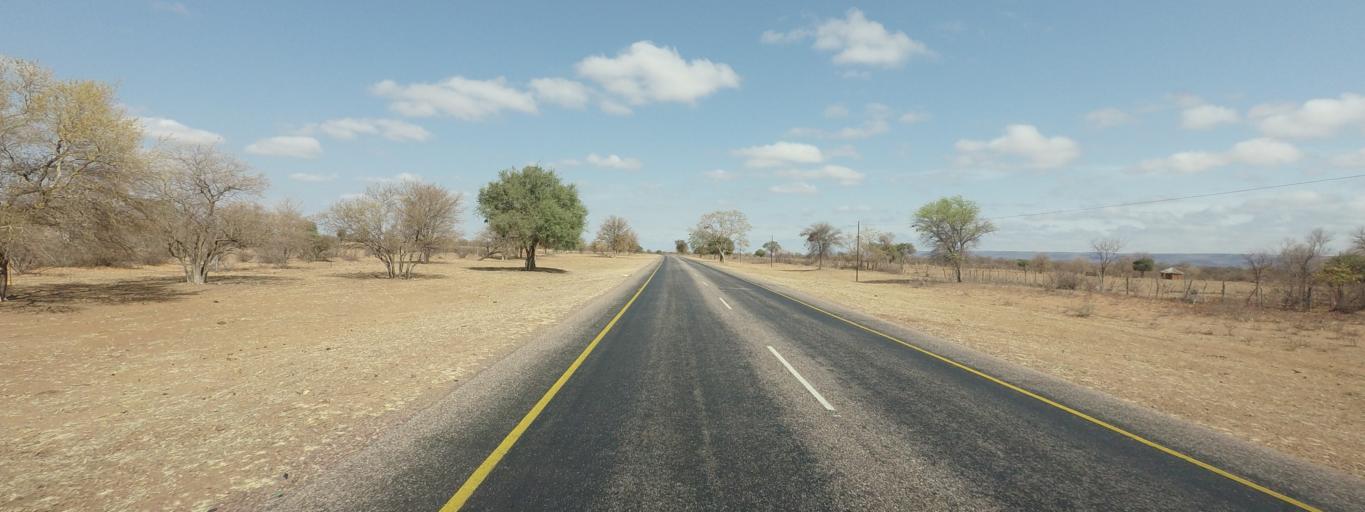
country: BW
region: Central
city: Ramokgonami
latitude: -22.7926
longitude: 27.4604
